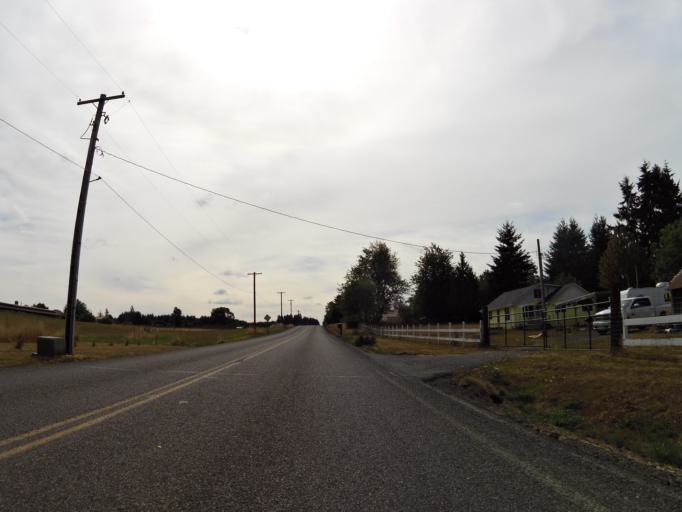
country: US
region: Washington
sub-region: Lewis County
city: Napavine
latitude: 46.5424
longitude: -122.9495
